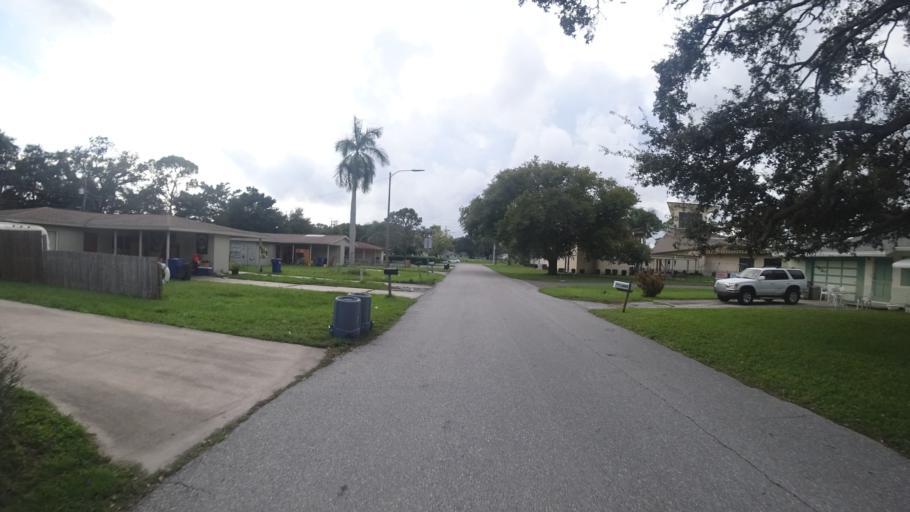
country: US
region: Florida
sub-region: Manatee County
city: South Bradenton
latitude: 27.4570
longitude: -82.5864
